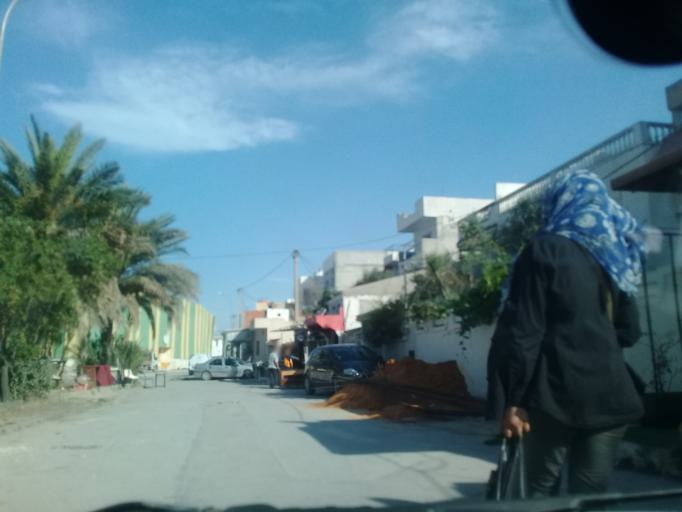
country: TN
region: Ariana
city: Ariana
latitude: 36.8332
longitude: 10.1949
